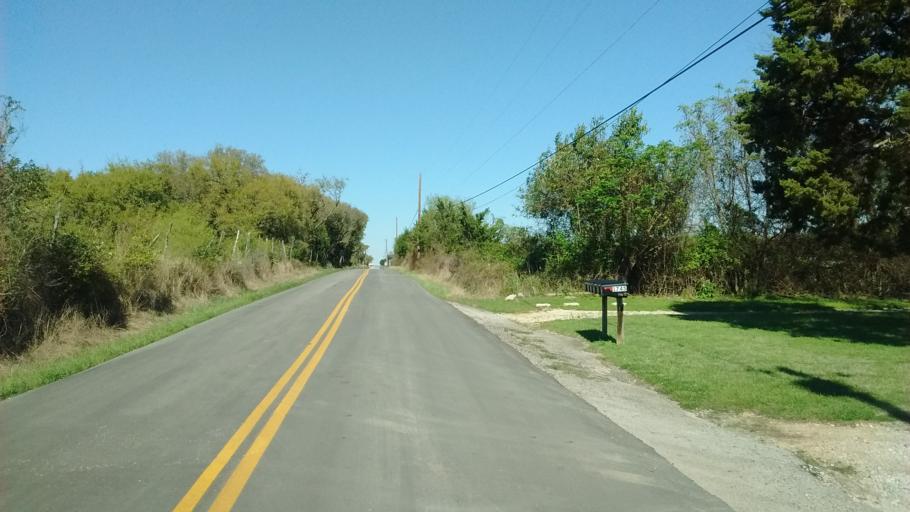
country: US
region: Texas
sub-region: Comal County
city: New Braunfels
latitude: 29.7162
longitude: -98.2103
